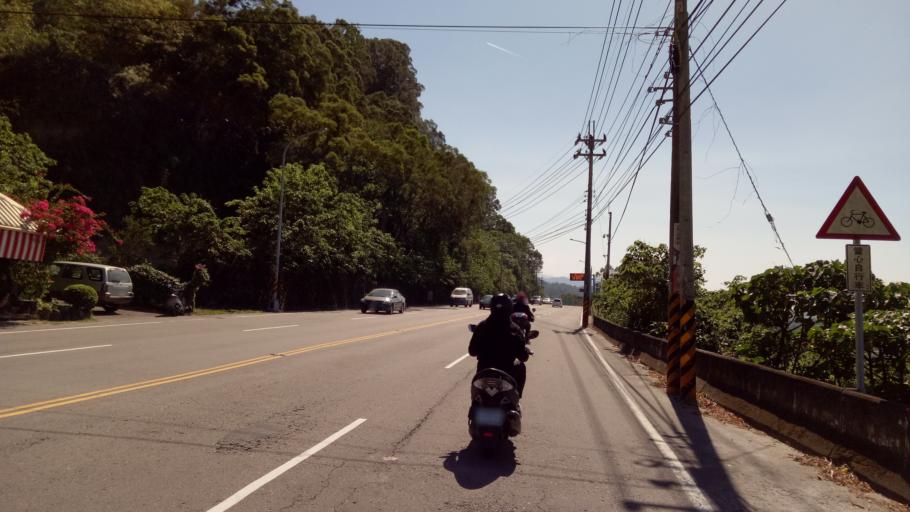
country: TW
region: Taiwan
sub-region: Hsinchu
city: Hsinchu
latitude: 24.6765
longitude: 120.9661
